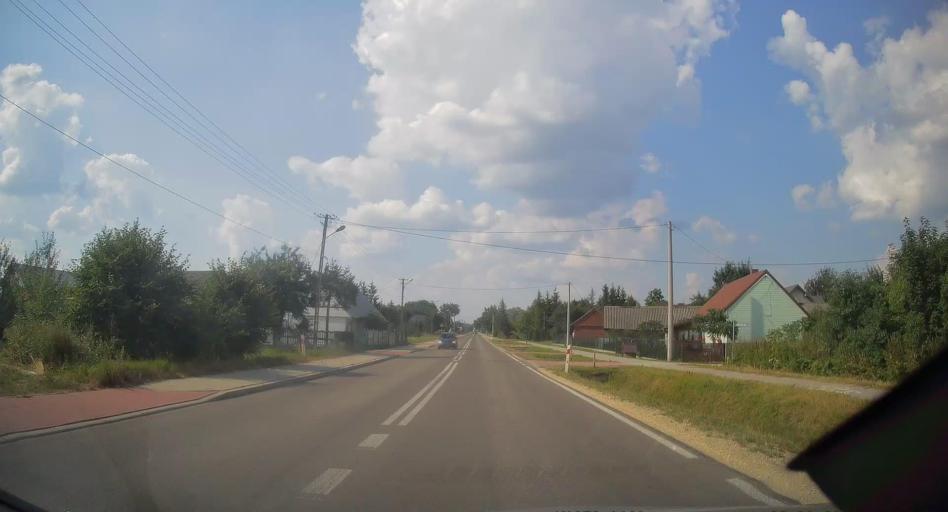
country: PL
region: Swietokrzyskie
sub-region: Powiat konecki
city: Radoszyce
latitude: 51.0464
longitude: 20.2836
